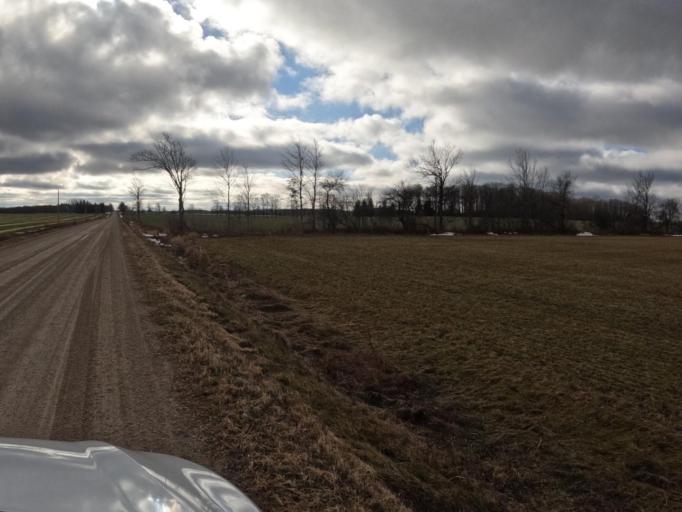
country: CA
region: Ontario
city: Shelburne
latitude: 43.9810
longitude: -80.3822
